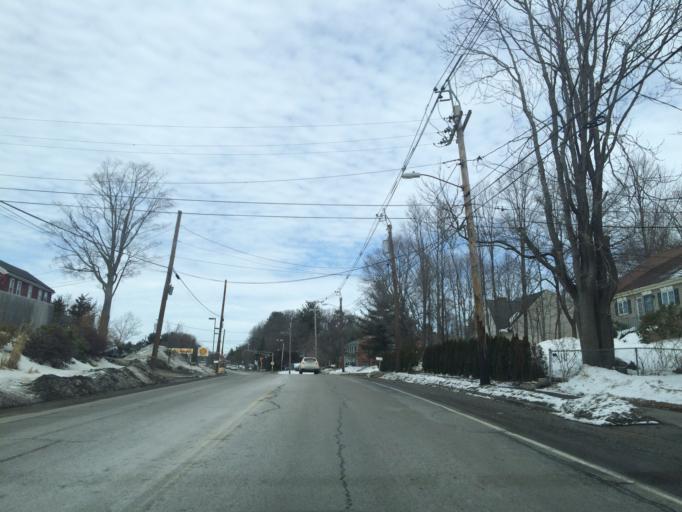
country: US
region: Massachusetts
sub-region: Middlesex County
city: Lexington
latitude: 42.4166
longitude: -71.2316
